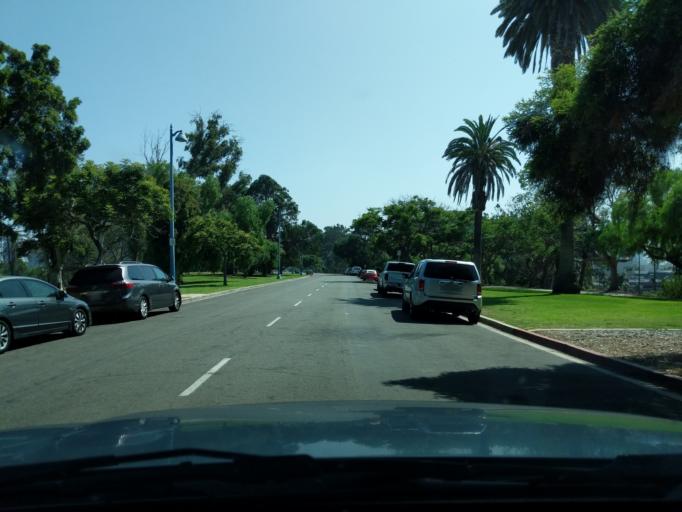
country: US
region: California
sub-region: San Diego County
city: San Diego
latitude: 32.7278
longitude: -117.1582
